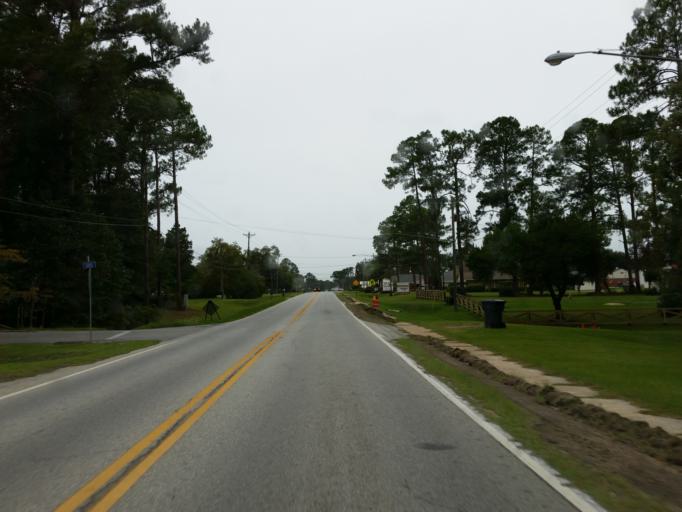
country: US
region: Georgia
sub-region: Lanier County
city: Lakeland
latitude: 31.0414
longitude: -83.0834
